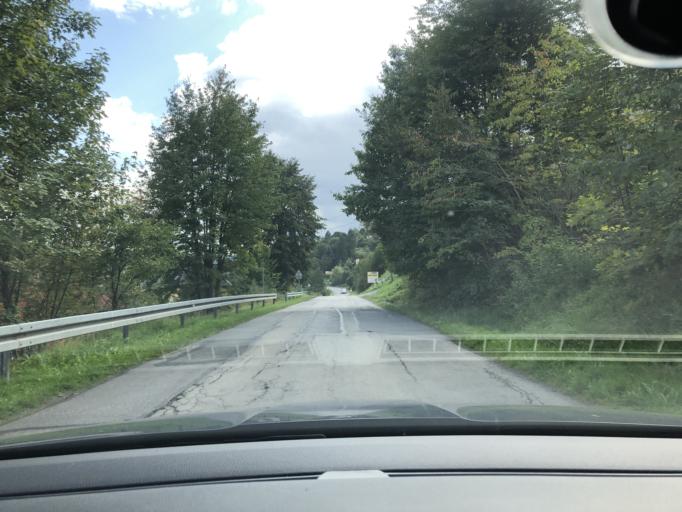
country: PL
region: Silesian Voivodeship
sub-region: Powiat zywiecki
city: Czernichow
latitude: 49.7407
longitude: 19.2056
